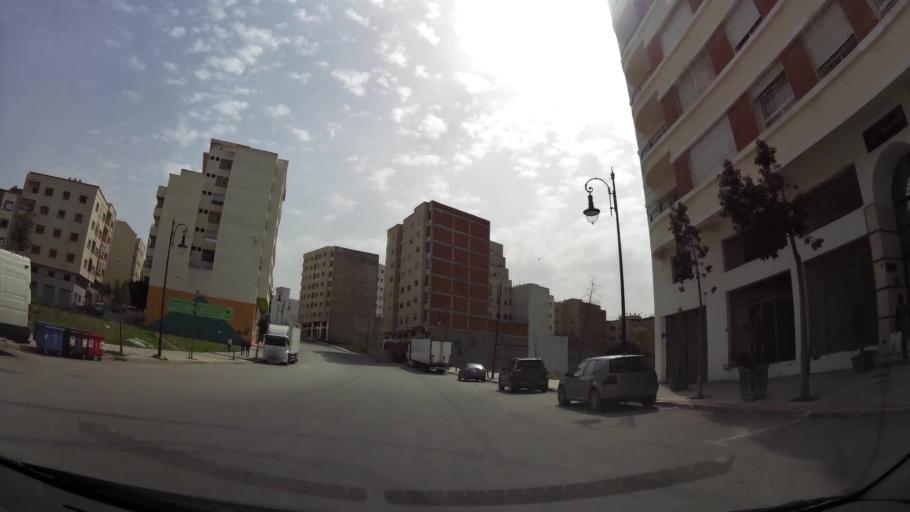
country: MA
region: Tanger-Tetouan
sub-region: Tanger-Assilah
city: Boukhalef
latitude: 35.7377
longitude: -5.8532
